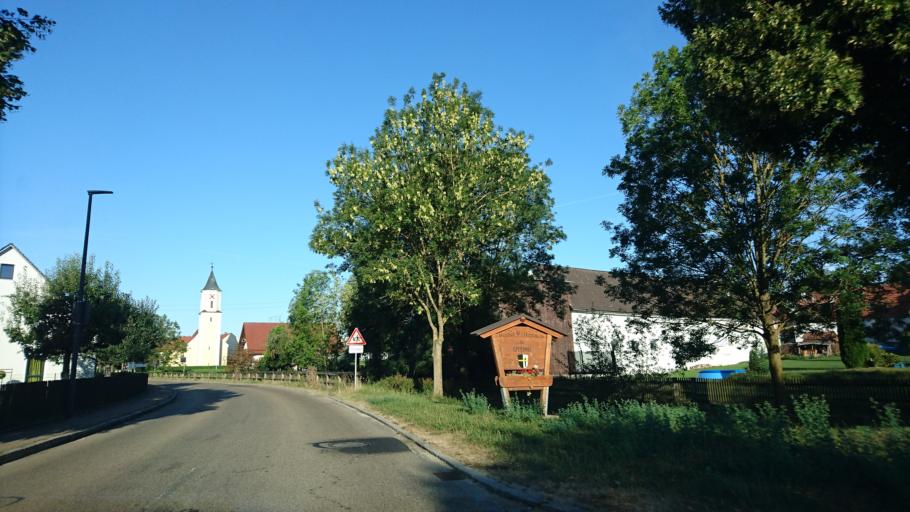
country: DE
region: Bavaria
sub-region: Swabia
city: Otting
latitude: 48.8737
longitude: 10.8062
